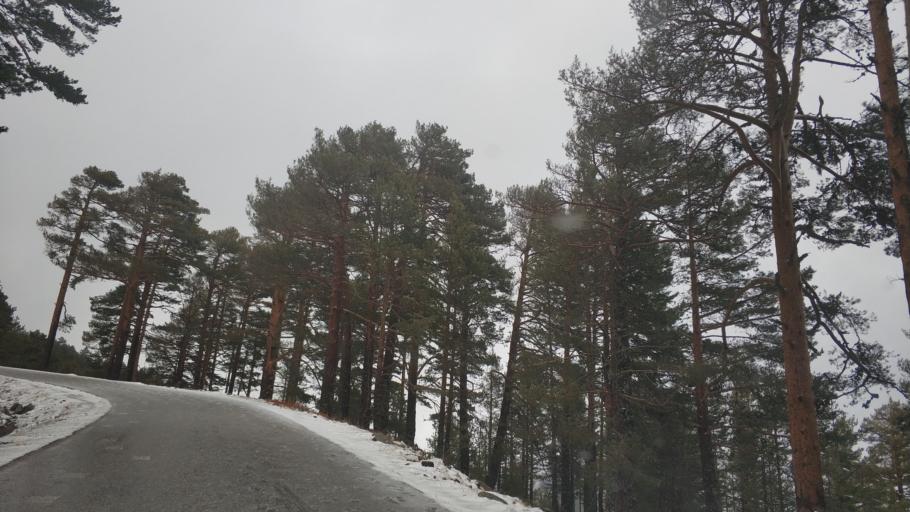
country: ES
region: Castille and Leon
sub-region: Provincia de Burgos
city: Neila
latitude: 42.0465
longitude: -3.0351
